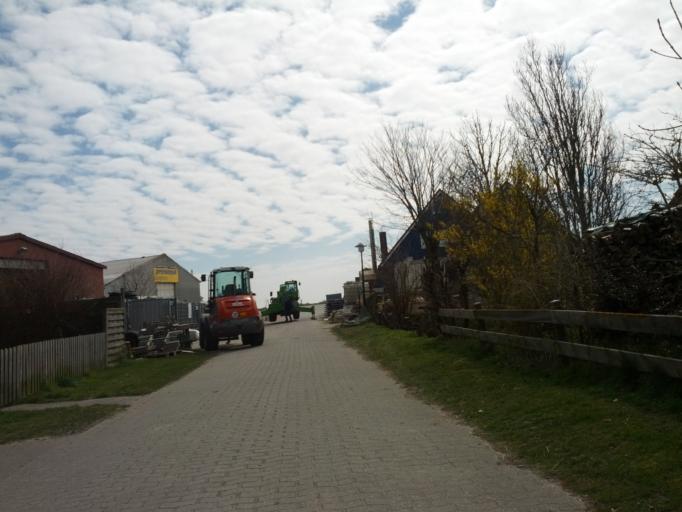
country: DE
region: Lower Saxony
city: Langeoog
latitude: 53.7460
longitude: 7.4933
